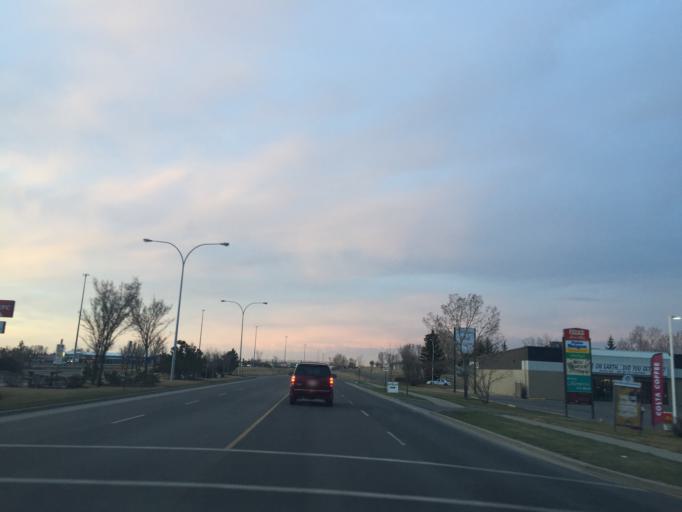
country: CA
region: Alberta
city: Airdrie
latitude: 51.2901
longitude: -114.0017
